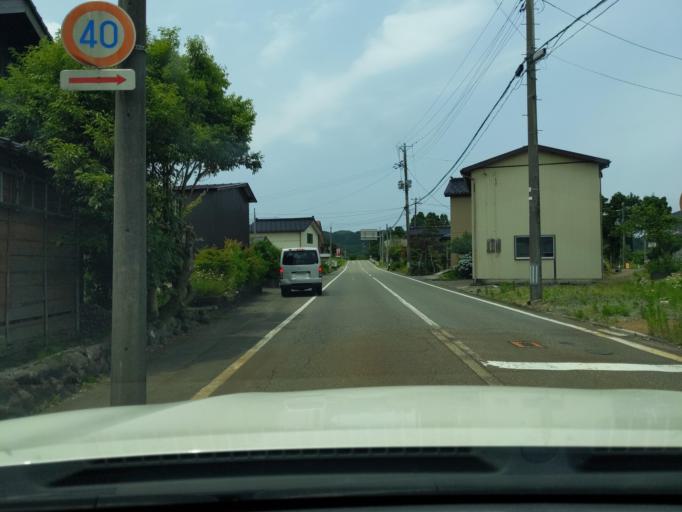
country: JP
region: Niigata
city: Kashiwazaki
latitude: 37.3316
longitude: 138.5638
